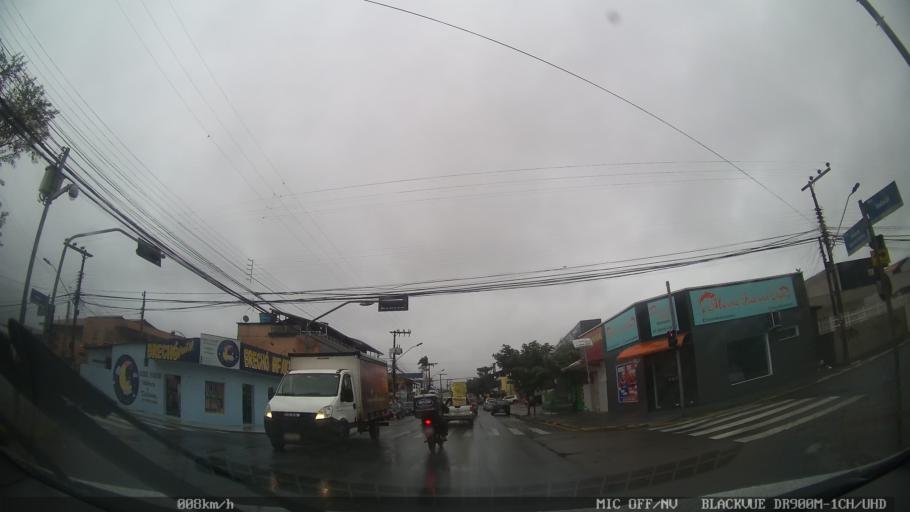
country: BR
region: Santa Catarina
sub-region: Itajai
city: Itajai
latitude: -26.9056
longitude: -48.6777
